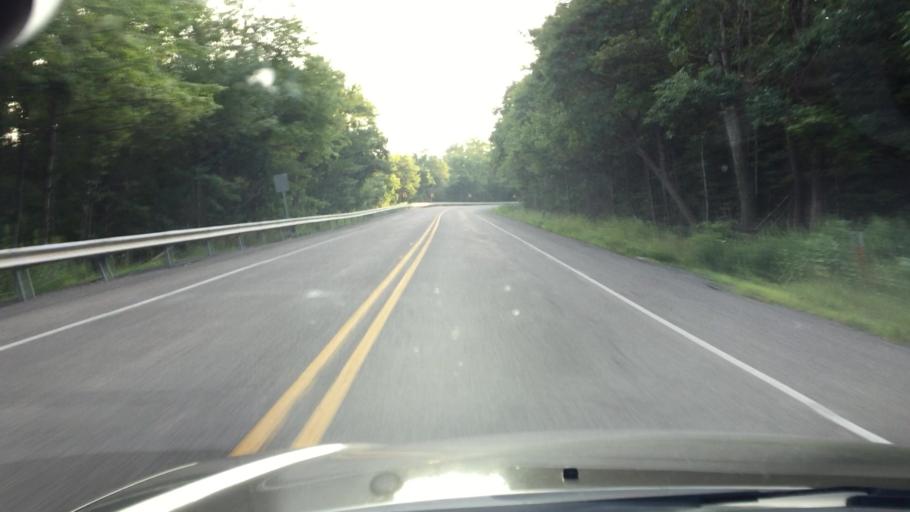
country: US
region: Pennsylvania
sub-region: Carbon County
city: Weatherly
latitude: 40.9257
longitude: -75.8874
